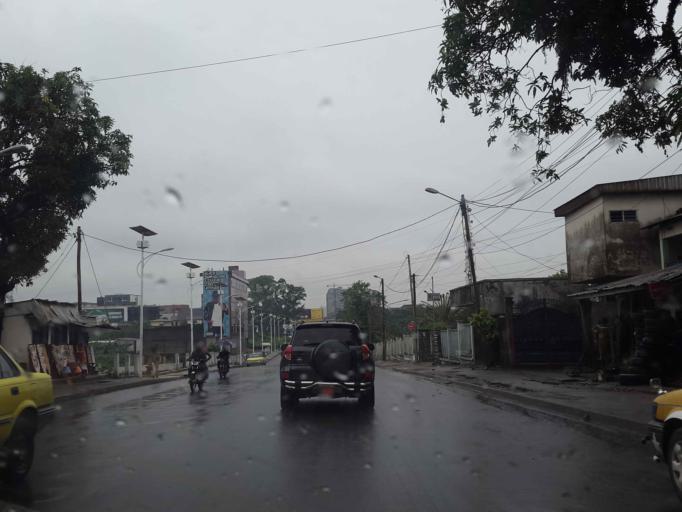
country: CM
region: Littoral
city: Douala
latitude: 4.0628
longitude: 9.7055
